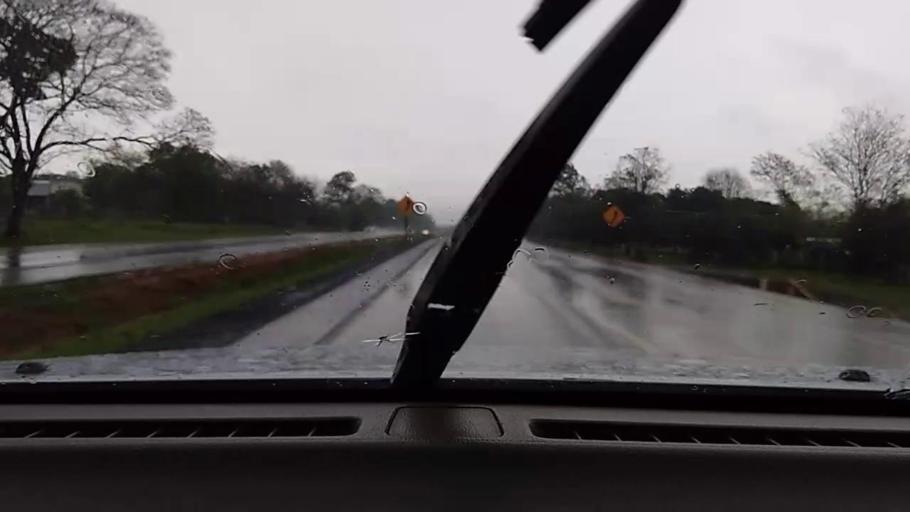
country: PY
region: Caaguazu
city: Repatriacion
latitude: -25.4535
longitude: -55.9078
